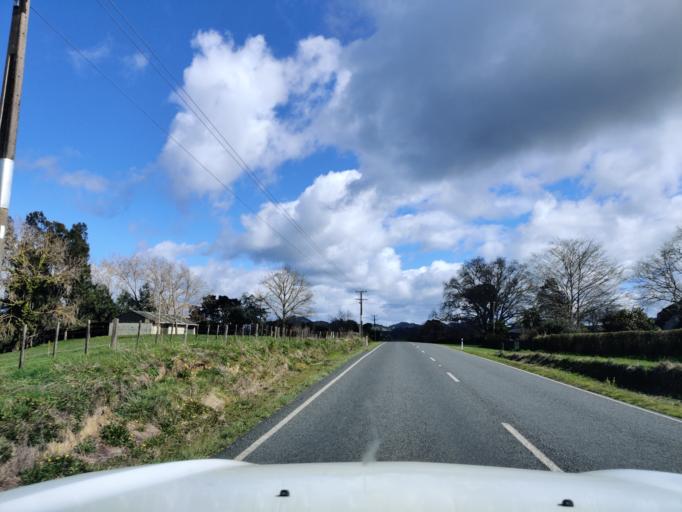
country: NZ
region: Waikato
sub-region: Waikato District
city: Ngaruawahia
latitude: -37.5721
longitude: 175.2496
